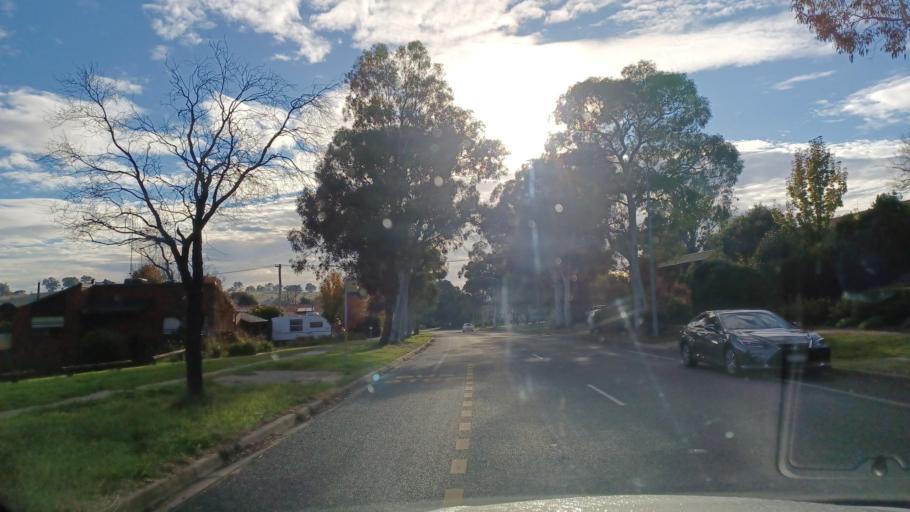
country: AU
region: Australian Capital Territory
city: Belconnen
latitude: -35.1910
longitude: 149.0454
